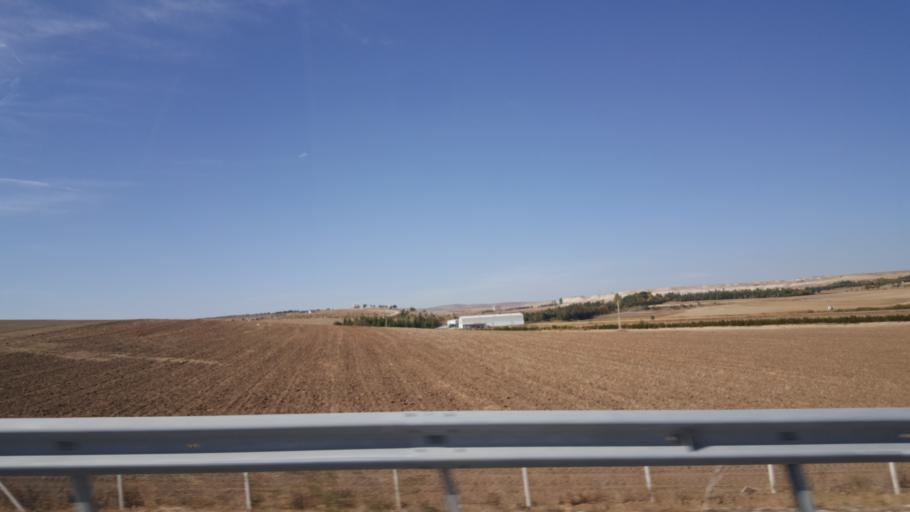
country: TR
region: Ankara
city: Ikizce
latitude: 39.6068
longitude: 32.6778
